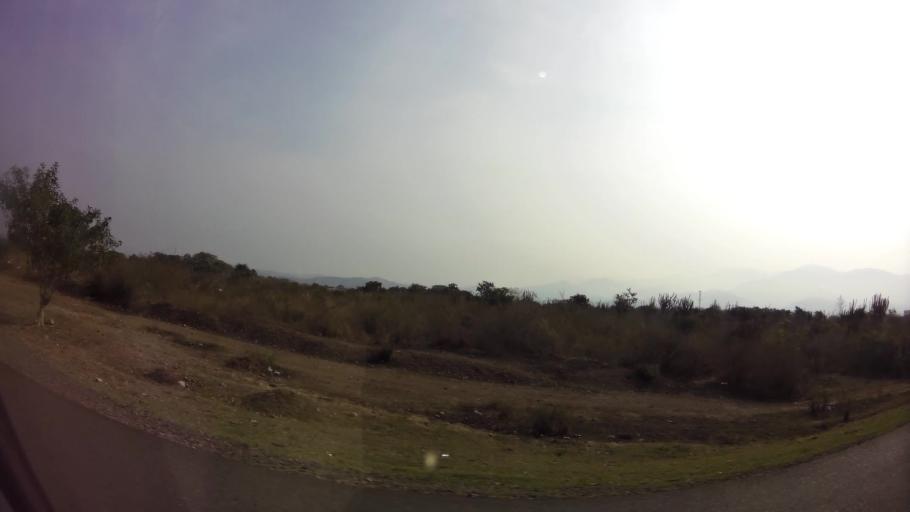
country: HN
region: Comayagua
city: Comayagua
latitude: 14.4288
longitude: -87.6407
